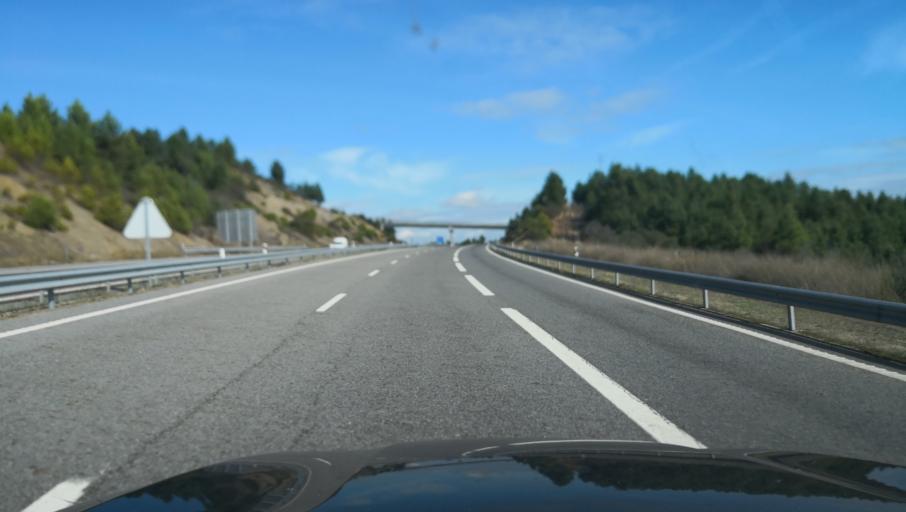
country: PT
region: Vila Real
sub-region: Chaves
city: Chaves
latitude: 41.6907
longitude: -7.5592
